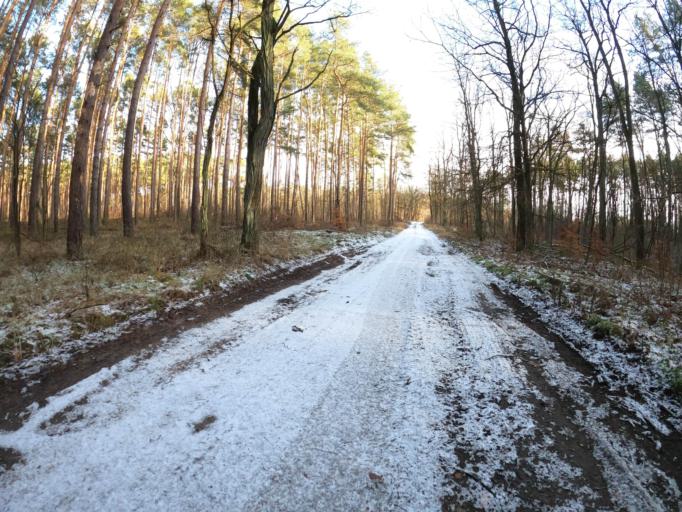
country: PL
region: Lubusz
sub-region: Powiat slubicki
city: Cybinka
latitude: 52.2290
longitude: 14.8378
